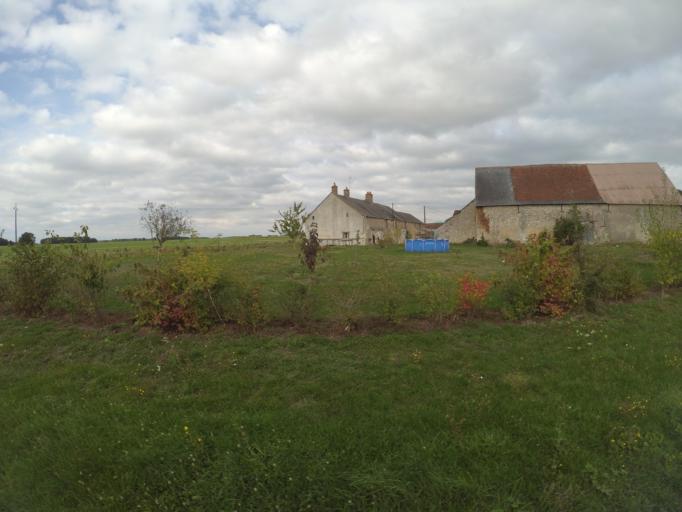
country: FR
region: Centre
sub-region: Departement d'Indre-et-Loire
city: Nazelles-Negron
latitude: 47.4697
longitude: 0.9374
